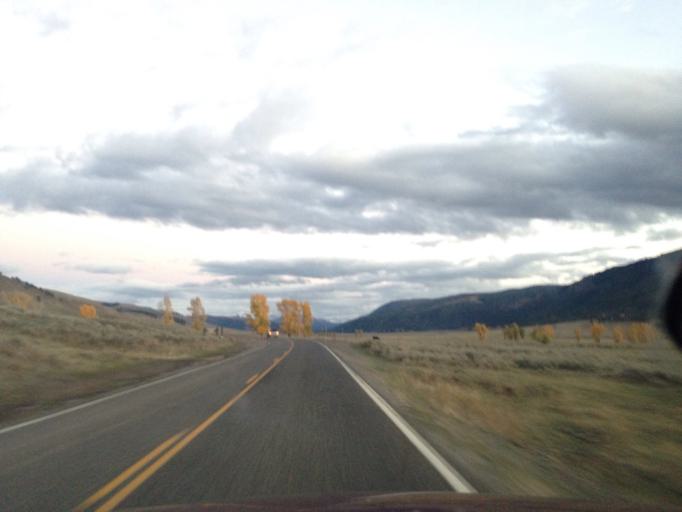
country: US
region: Montana
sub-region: Park County
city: Livingston
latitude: 44.8952
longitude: -110.2360
